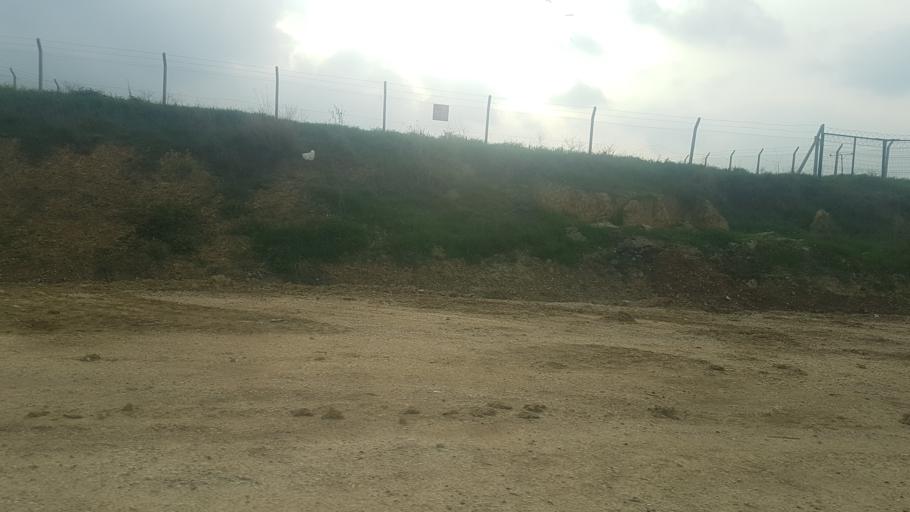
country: TR
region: Adana
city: Seyhan
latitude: 37.0493
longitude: 35.2096
